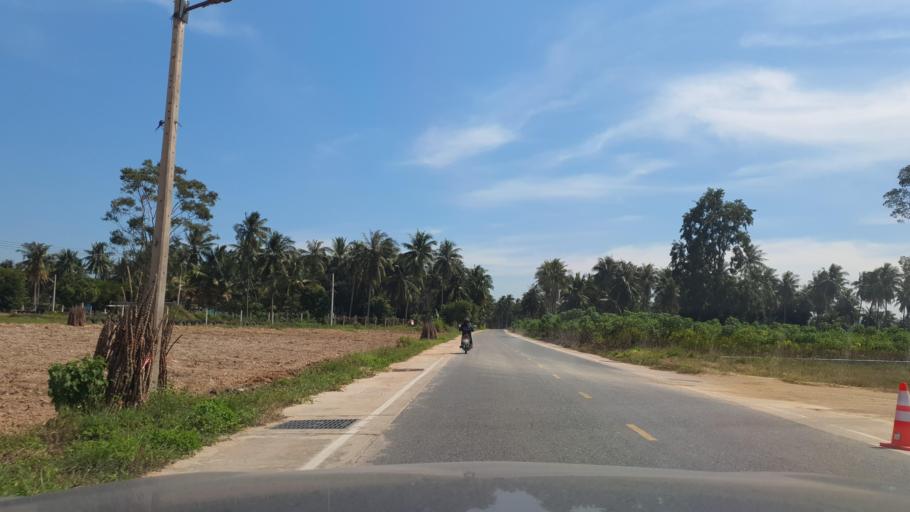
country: TH
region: Chon Buri
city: Bang Lamung
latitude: 12.9843
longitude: 100.9810
